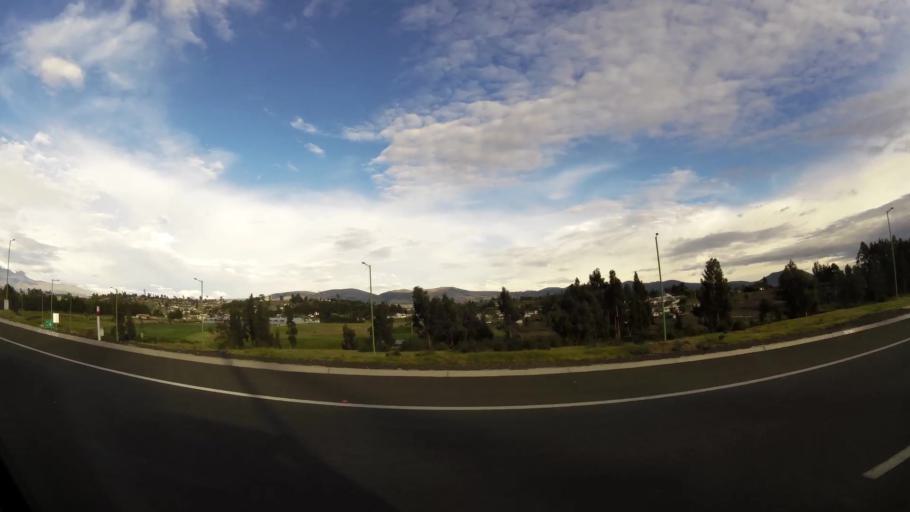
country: EC
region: Cotopaxi
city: Saquisili
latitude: -0.8534
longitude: -78.6198
